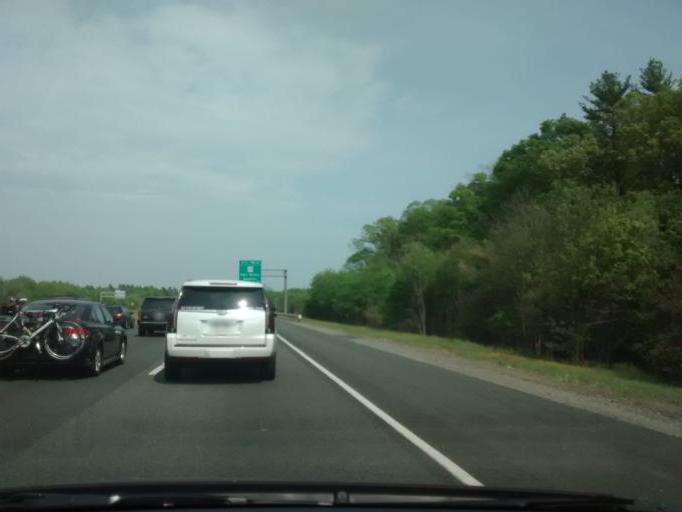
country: US
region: Massachusetts
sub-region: Bristol County
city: Raynham
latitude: 41.9582
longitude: -71.0593
